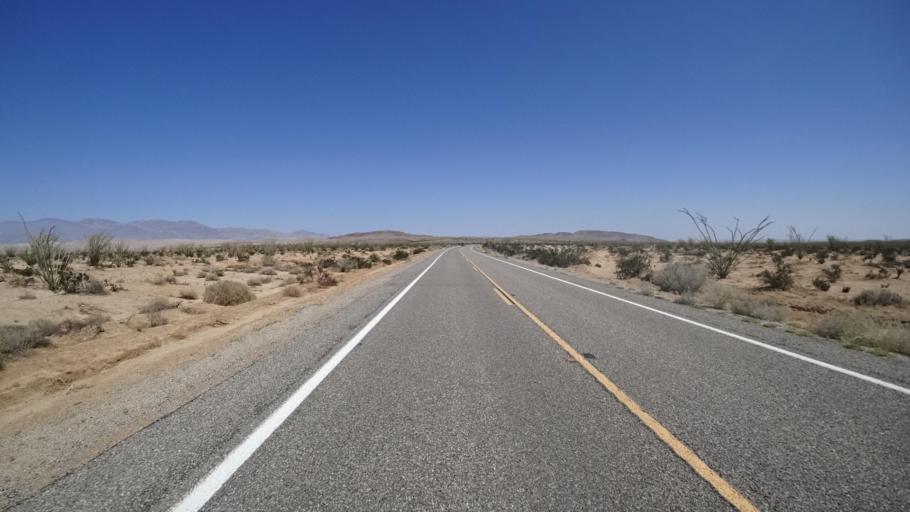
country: US
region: California
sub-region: San Diego County
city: Borrego Springs
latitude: 33.1557
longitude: -116.2484
